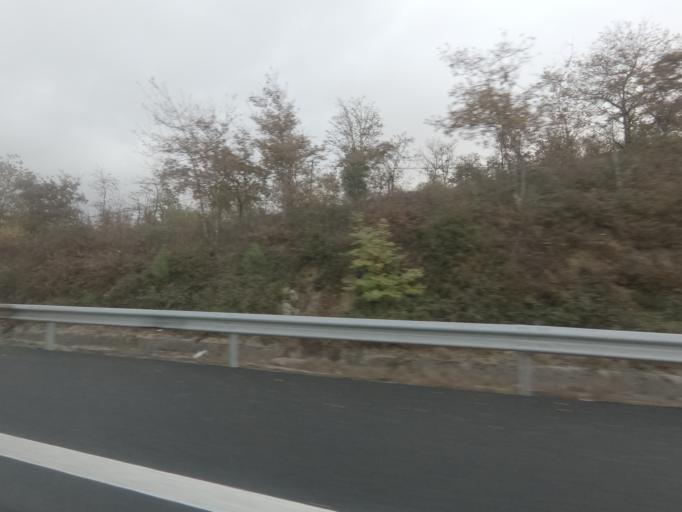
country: ES
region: Galicia
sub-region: Provincia de Pontevedra
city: Porrino
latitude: 42.2006
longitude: -8.6675
